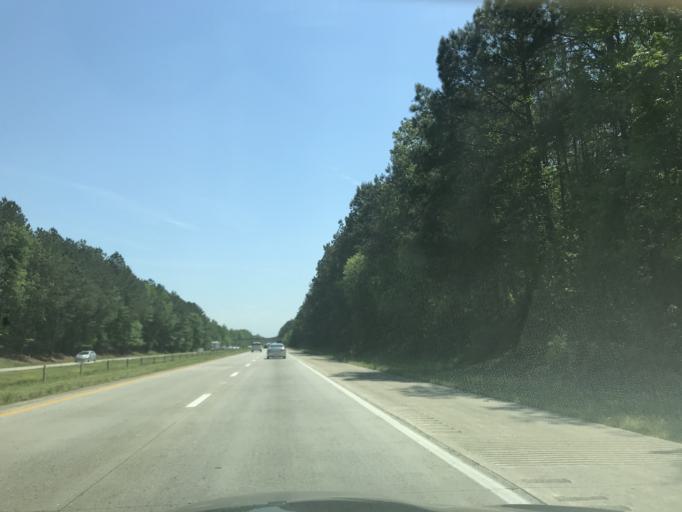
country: US
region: North Carolina
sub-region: Johnston County
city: Benson
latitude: 35.4947
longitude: -78.5533
